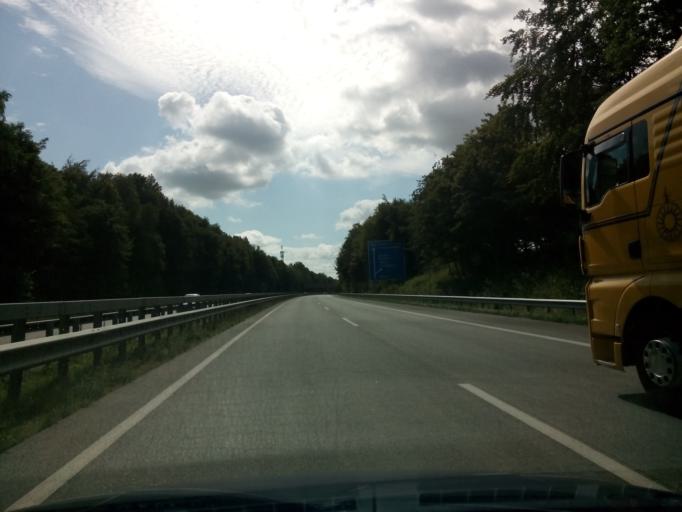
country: DE
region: Lower Saxony
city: Ritterhude
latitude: 53.1960
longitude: 8.6926
